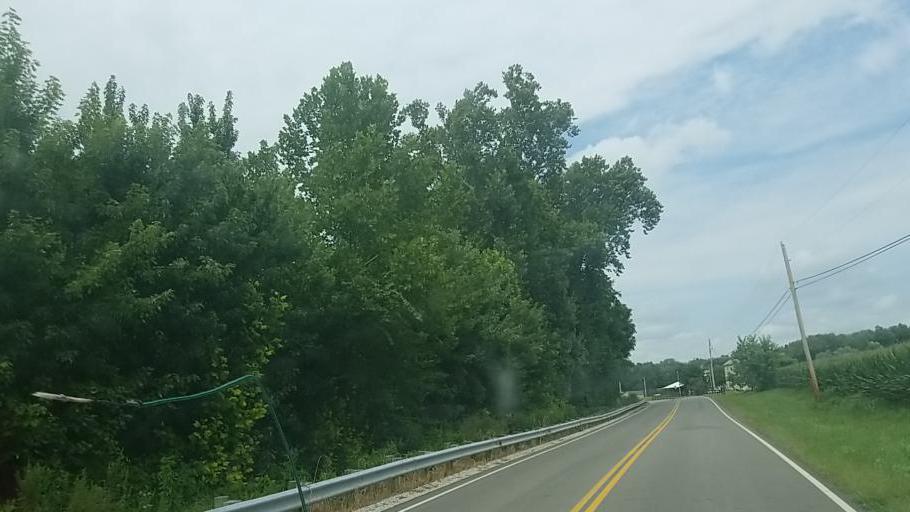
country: US
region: Ohio
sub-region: Pickaway County
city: Ashville
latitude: 39.7351
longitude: -82.9175
